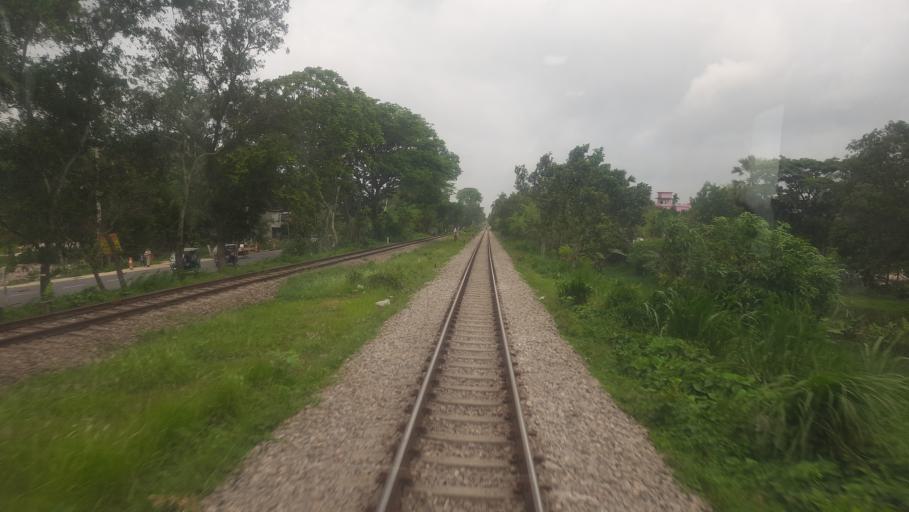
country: BD
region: Dhaka
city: Narsingdi
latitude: 23.9316
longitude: 90.7341
